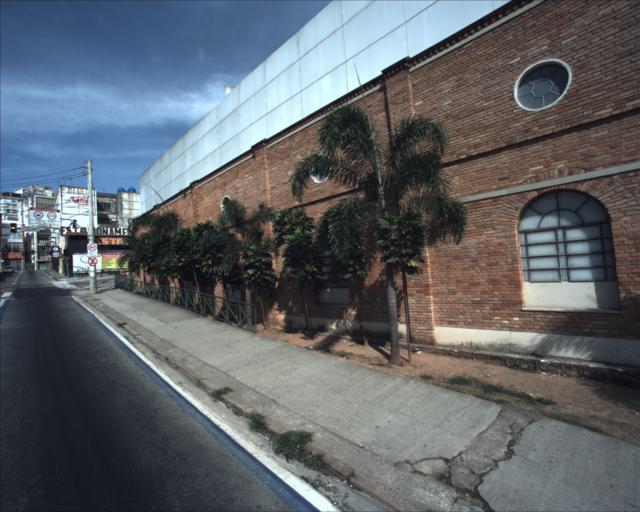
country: BR
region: Sao Paulo
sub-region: Sorocaba
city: Sorocaba
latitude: -23.4969
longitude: -47.4583
